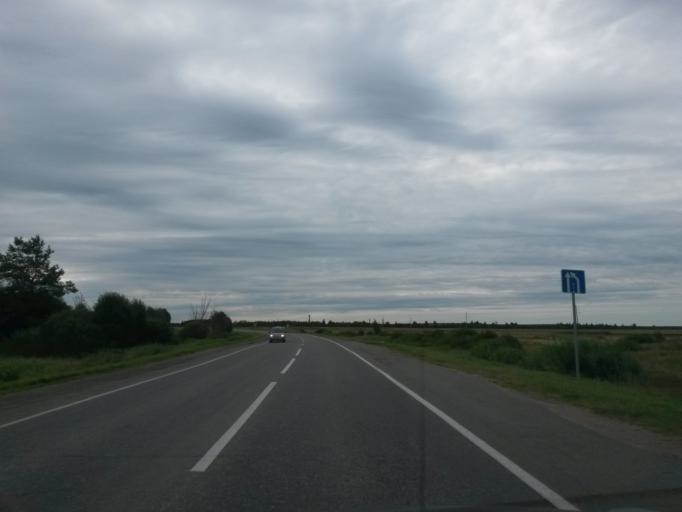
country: RU
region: Jaroslavl
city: Gavrilov-Yam
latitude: 57.3305
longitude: 39.8151
